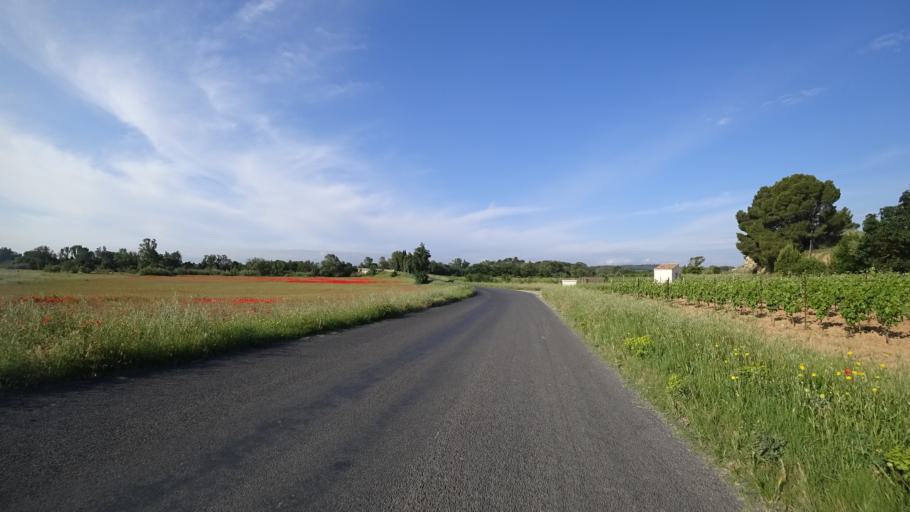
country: FR
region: Languedoc-Roussillon
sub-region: Departement de l'Aude
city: Canet
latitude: 43.2407
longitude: 2.7989
